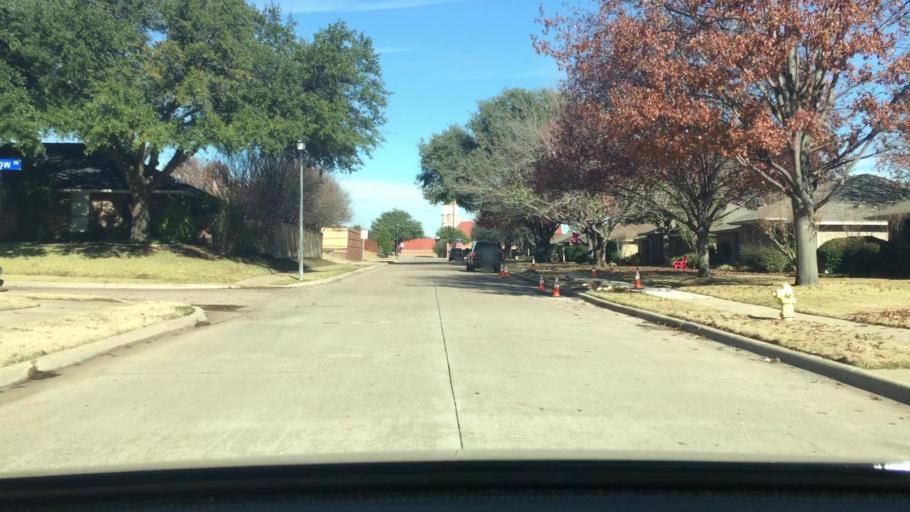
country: US
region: Texas
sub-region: Dallas County
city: Coppell
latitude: 32.9678
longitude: -96.9702
